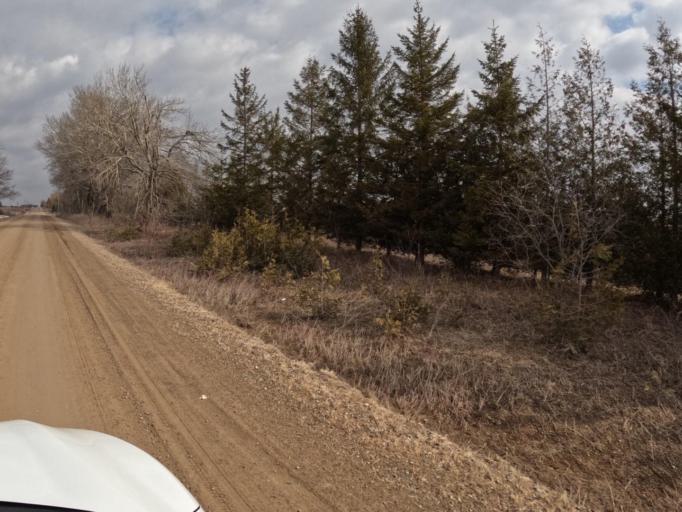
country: CA
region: Ontario
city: Orangeville
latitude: 43.9202
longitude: -80.1855
